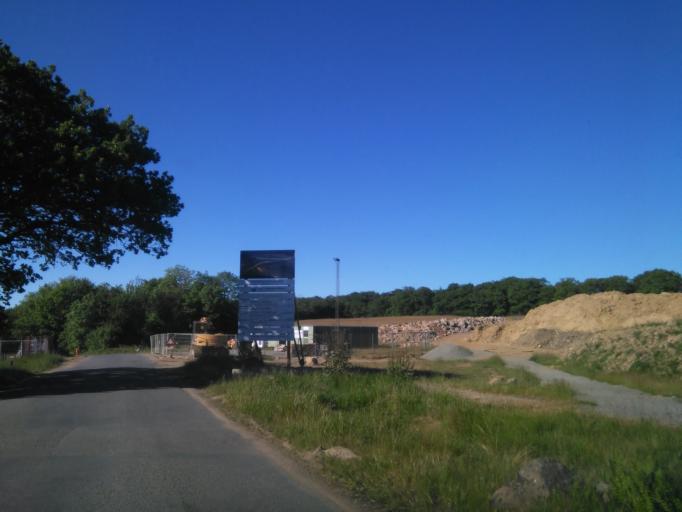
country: DK
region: Capital Region
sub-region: Bornholm Kommune
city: Ronne
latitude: 55.2709
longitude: 14.7625
